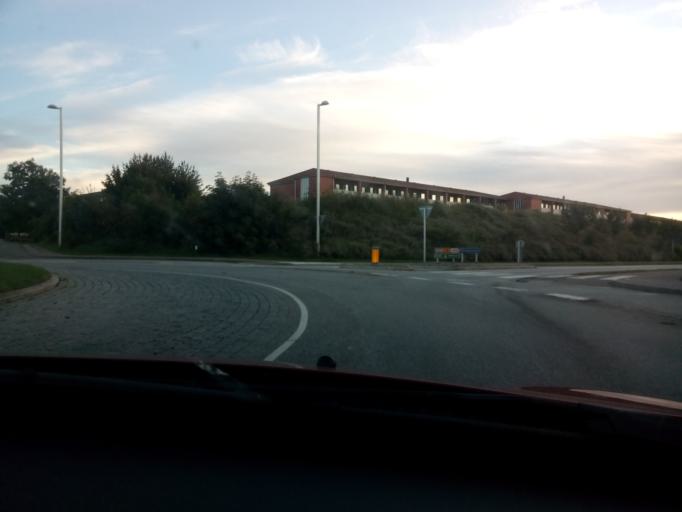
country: DK
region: Central Jutland
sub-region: Randers Kommune
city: Randers
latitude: 56.4823
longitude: 10.0417
